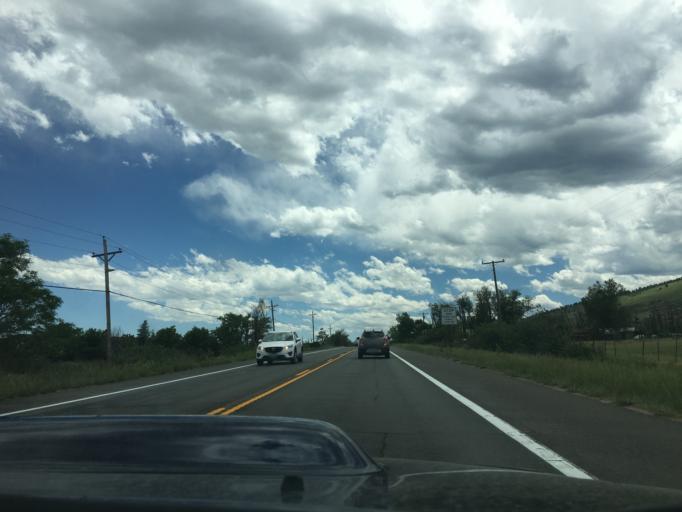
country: US
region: Colorado
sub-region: Boulder County
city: Lyons
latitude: 40.2056
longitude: -105.2494
